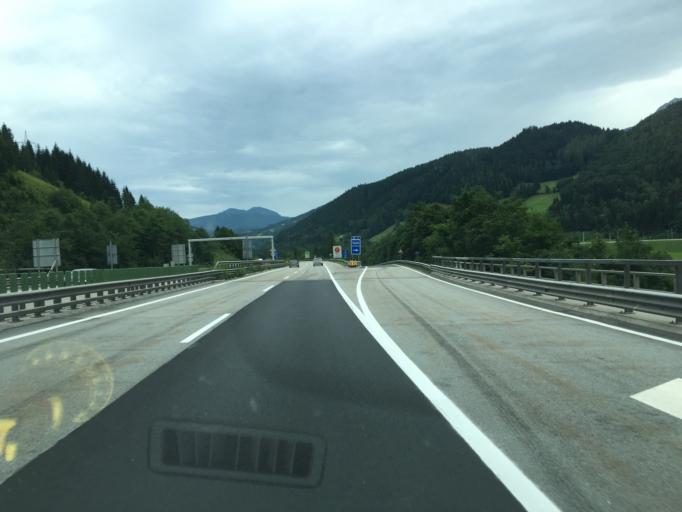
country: AT
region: Styria
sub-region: Politischer Bezirk Liezen
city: Ardning
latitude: 47.6442
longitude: 14.3313
